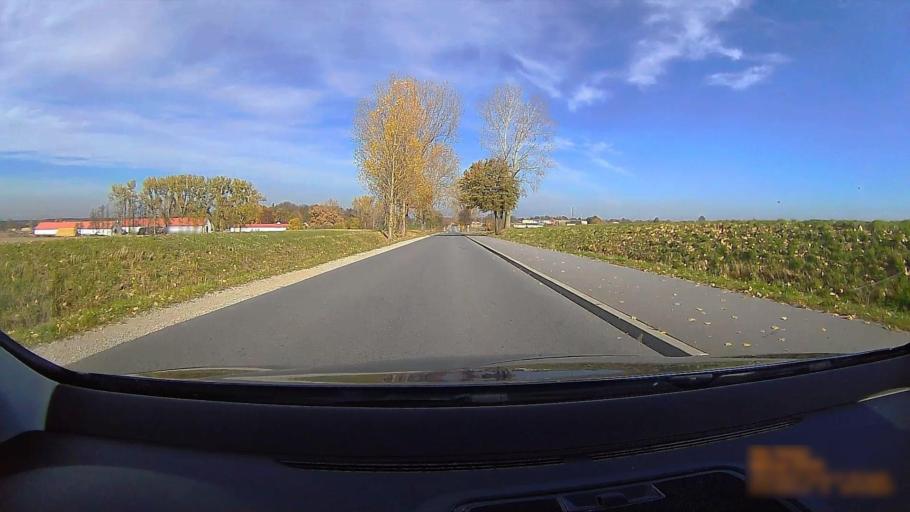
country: PL
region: Greater Poland Voivodeship
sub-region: Powiat kepinski
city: Kepno
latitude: 51.3411
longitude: 18.0223
